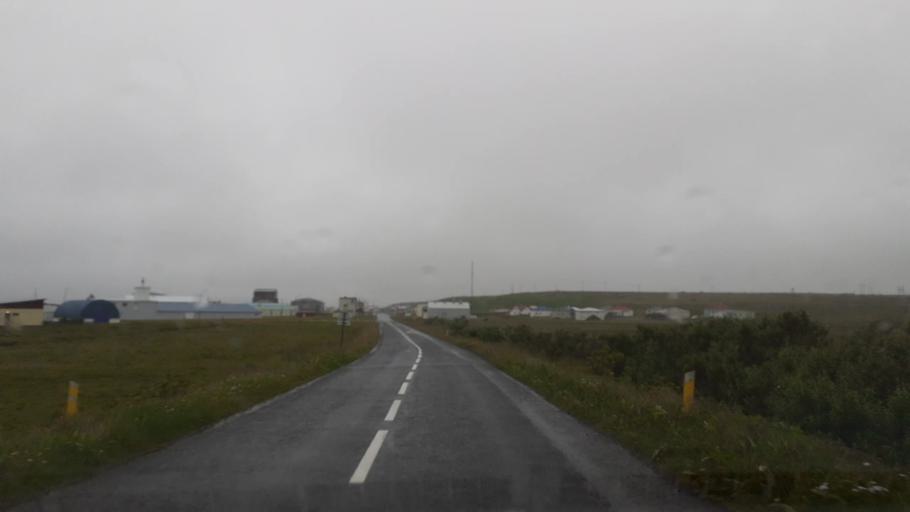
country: IS
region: Northeast
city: Husavik
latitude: 66.4593
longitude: -15.9519
